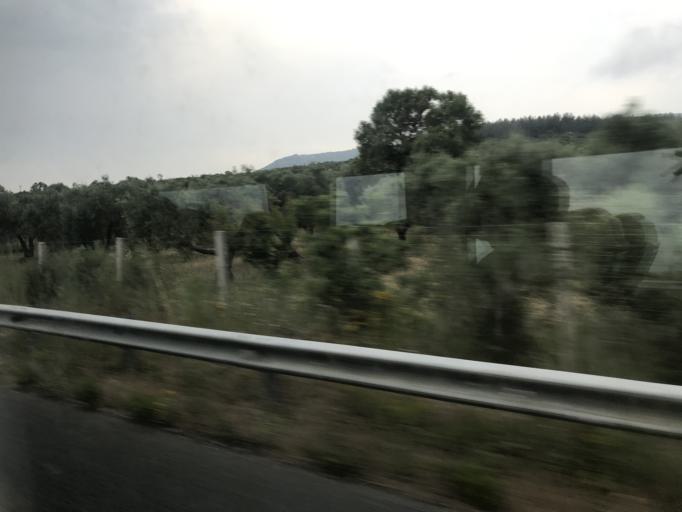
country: GR
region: East Macedonia and Thrace
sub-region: Nomos Evrou
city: Alexandroupoli
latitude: 40.8628
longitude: 25.7607
